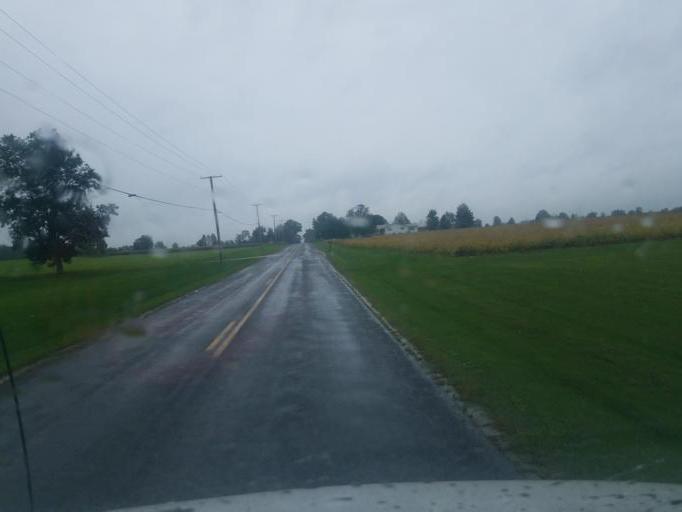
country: US
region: Ohio
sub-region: Medina County
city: Seville
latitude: 41.0186
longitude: -81.8326
